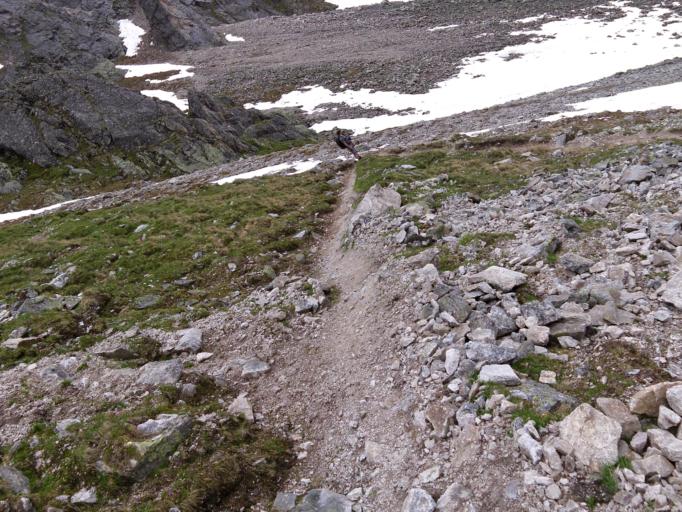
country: AT
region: Tyrol
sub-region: Politischer Bezirk Innsbruck Land
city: Neustift im Stubaital
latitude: 47.0700
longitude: 11.2065
